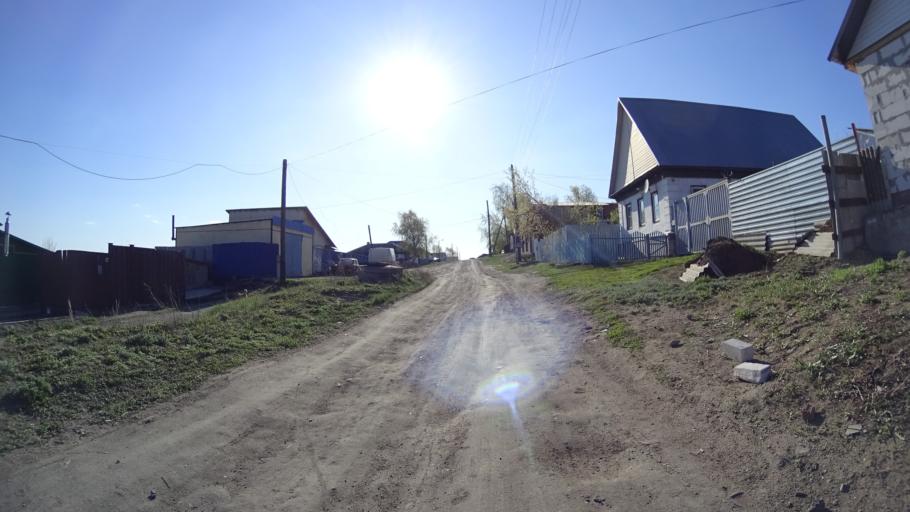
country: RU
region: Chelyabinsk
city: Troitsk
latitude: 54.0992
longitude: 61.5471
